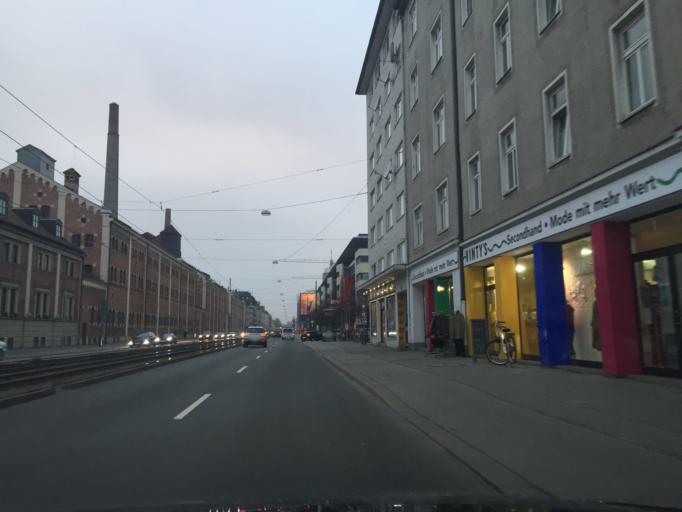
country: DE
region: Bavaria
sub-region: Upper Bavaria
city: Munich
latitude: 48.1394
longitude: 11.5461
